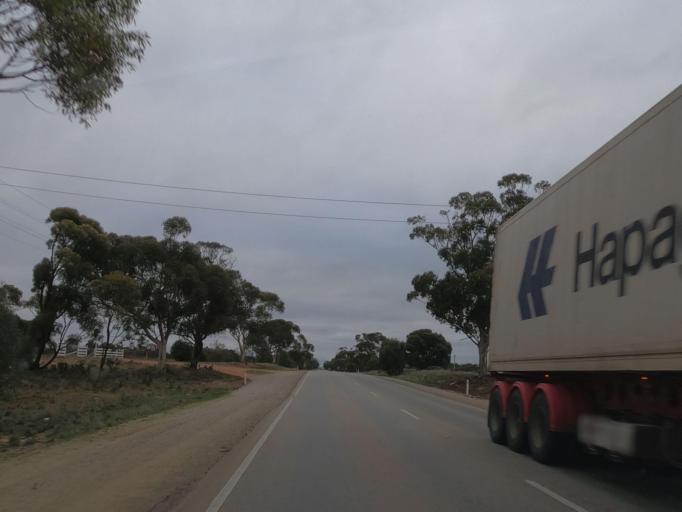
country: AU
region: Victoria
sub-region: Swan Hill
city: Swan Hill
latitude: -35.4068
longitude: 143.5820
